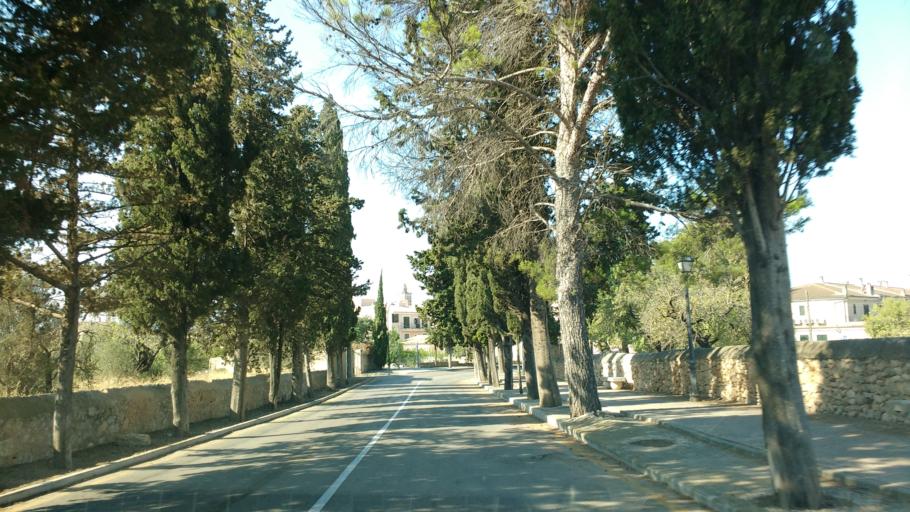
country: ES
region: Balearic Islands
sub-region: Illes Balears
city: Consell
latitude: 39.6715
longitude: 2.8145
